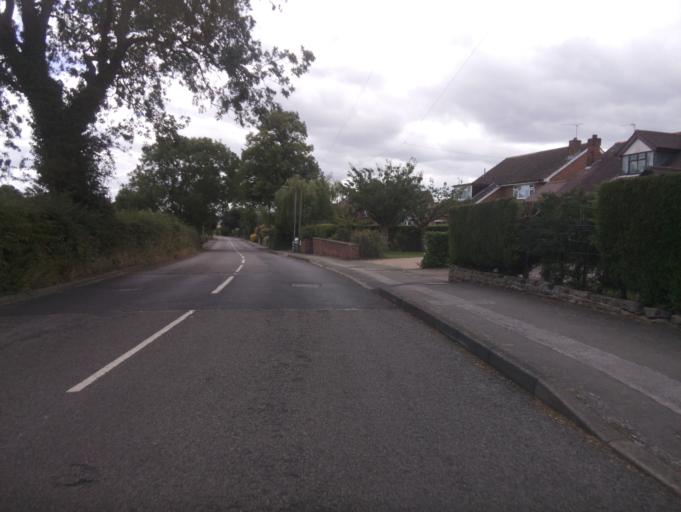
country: GB
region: England
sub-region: Nottinghamshire
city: West Bridgford
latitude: 52.9006
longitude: -1.0938
